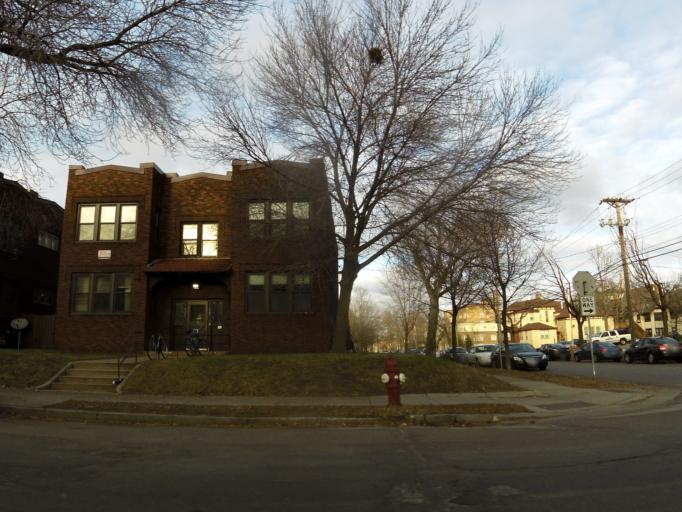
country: US
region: Minnesota
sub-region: Hennepin County
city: Minneapolis
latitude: 44.9834
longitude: -93.2465
